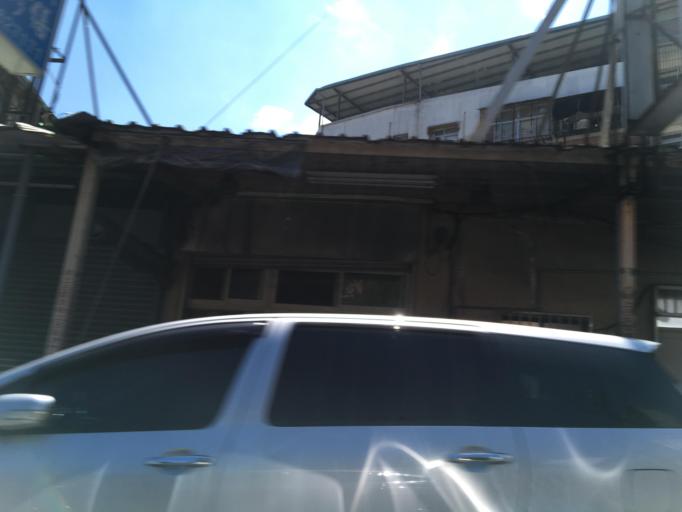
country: TW
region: Taipei
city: Taipei
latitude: 25.1450
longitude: 121.4959
